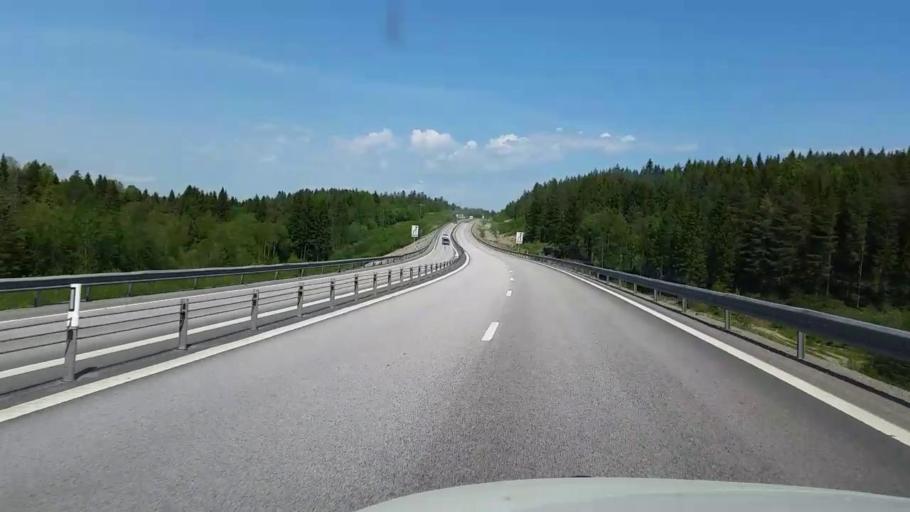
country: SE
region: Gaevleborg
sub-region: Hudiksvalls Kommun
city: Hudiksvall
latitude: 61.7261
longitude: 17.0648
